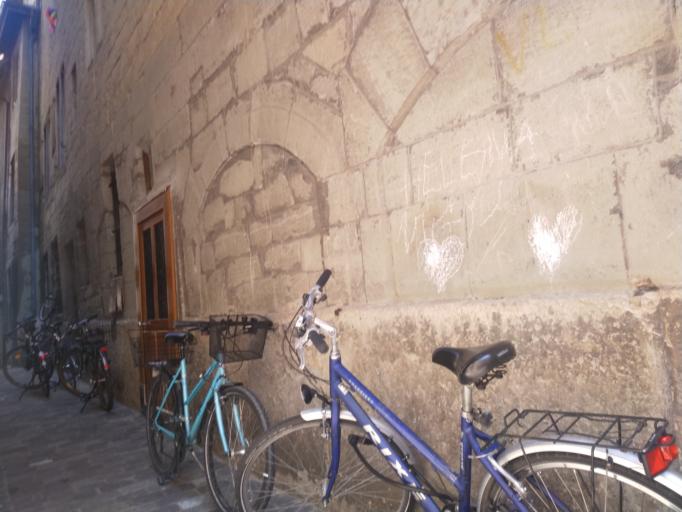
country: CH
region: Fribourg
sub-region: Sarine District
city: Fribourg
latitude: 46.8055
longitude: 7.1629
